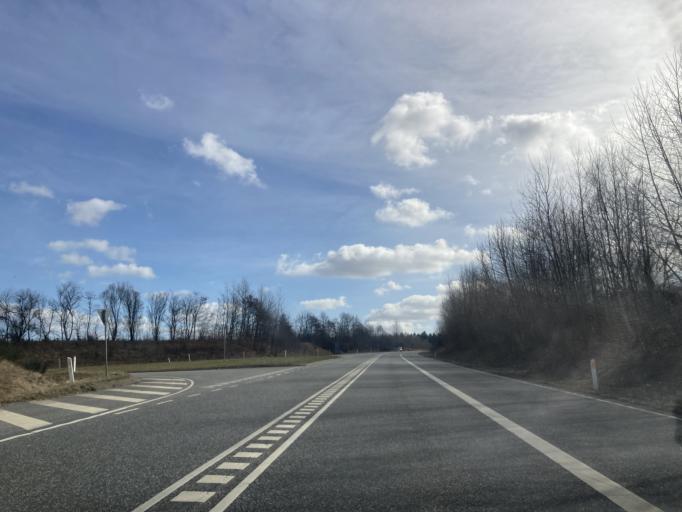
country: DK
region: Central Jutland
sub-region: Hedensted Kommune
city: Torring
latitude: 55.9682
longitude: 9.4030
